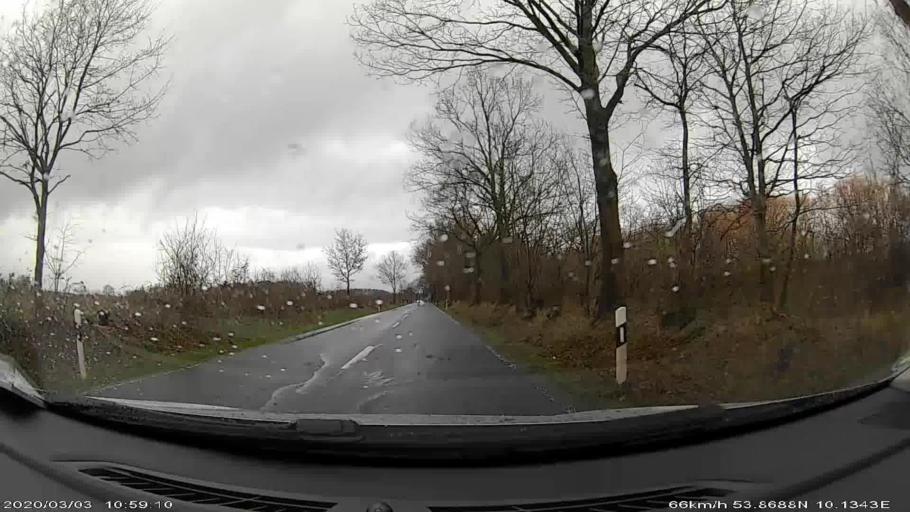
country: DE
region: Schleswig-Holstein
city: Stuvenborn
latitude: 53.8712
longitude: 10.1371
